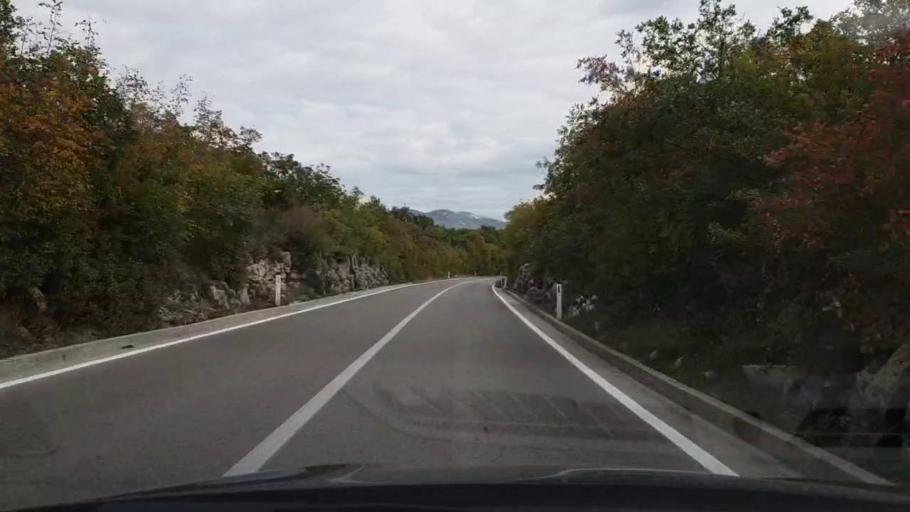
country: BA
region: Republika Srpska
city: Trebinje
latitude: 42.6874
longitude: 18.2827
